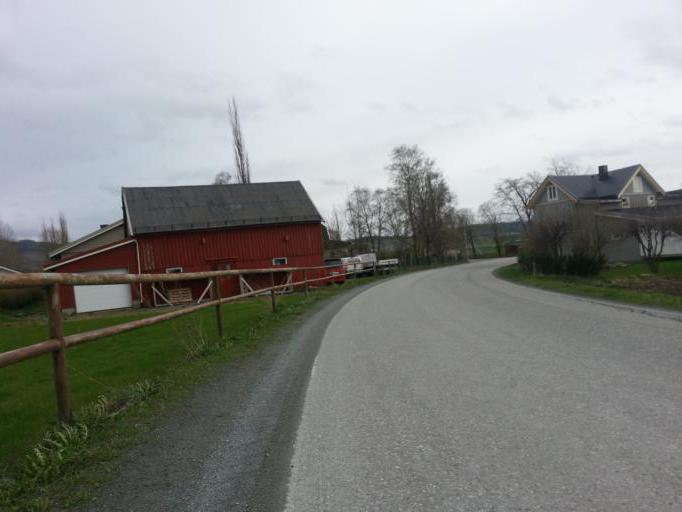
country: NO
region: Nord-Trondelag
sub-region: Levanger
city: Skogn
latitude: 63.6961
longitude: 11.1996
